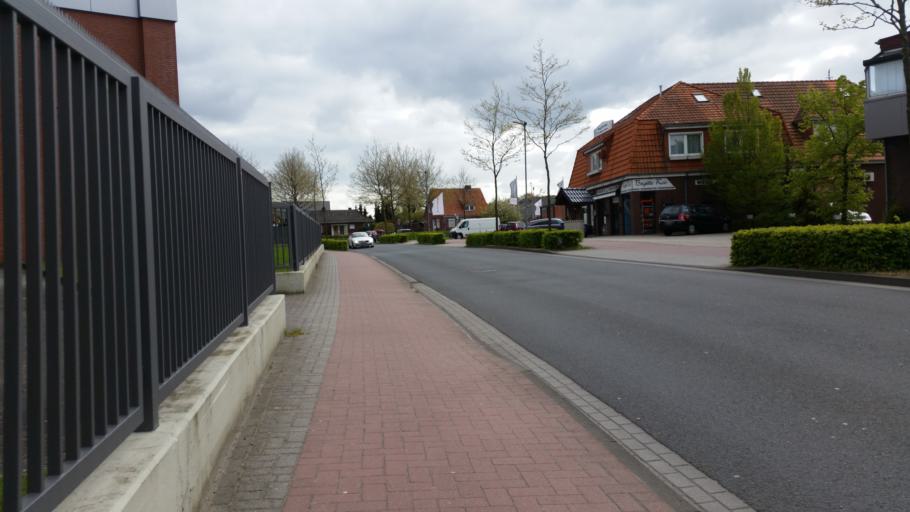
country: DE
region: Lower Saxony
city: Aurich
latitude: 53.4733
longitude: 7.4693
